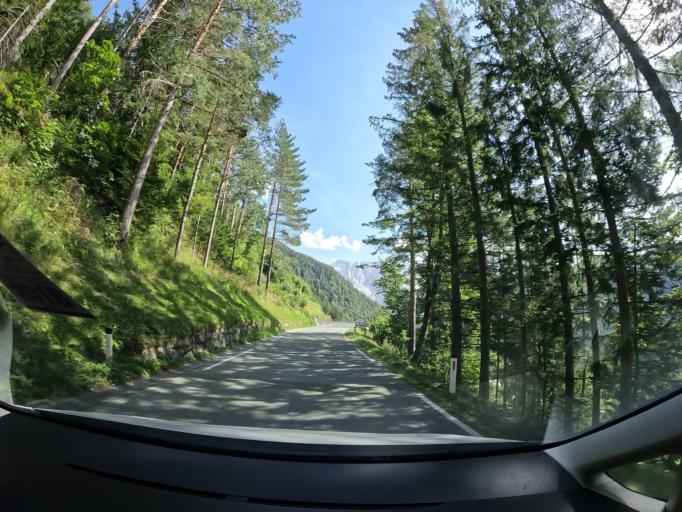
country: AT
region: Carinthia
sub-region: Politischer Bezirk Feldkirchen
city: Glanegg
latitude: 46.7431
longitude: 14.2052
